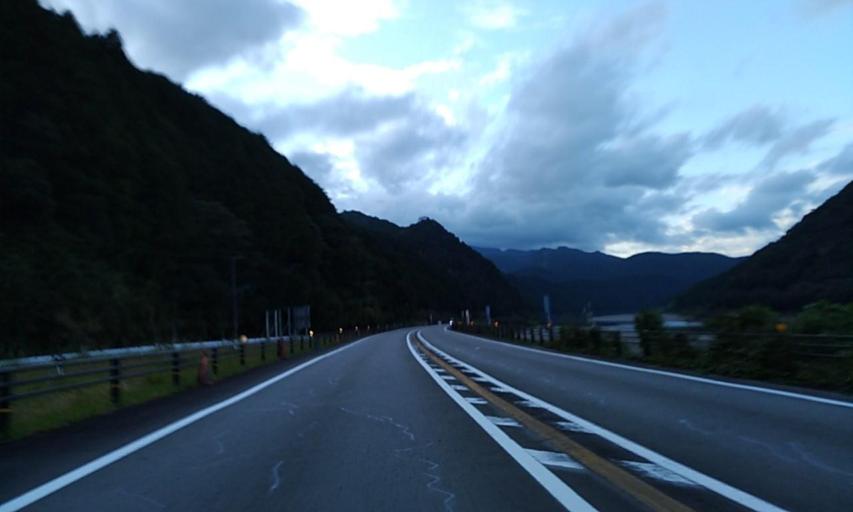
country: JP
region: Wakayama
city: Shingu
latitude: 33.7256
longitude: 135.9565
